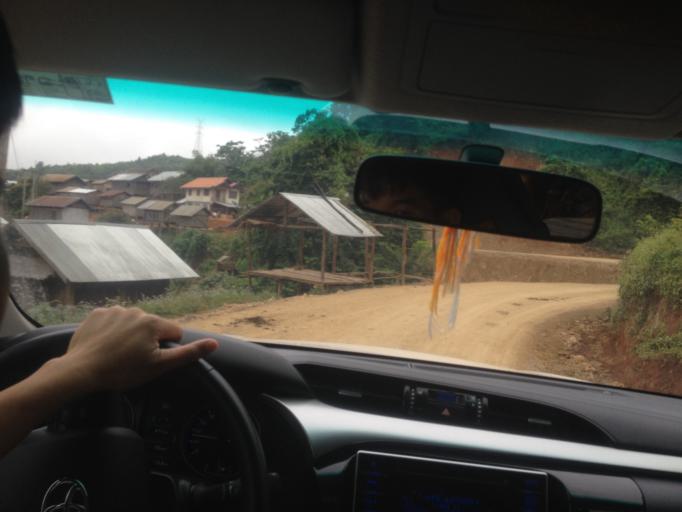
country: TH
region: Nan
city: Chaloem Phra Kiat
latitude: 19.9830
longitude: 101.1439
